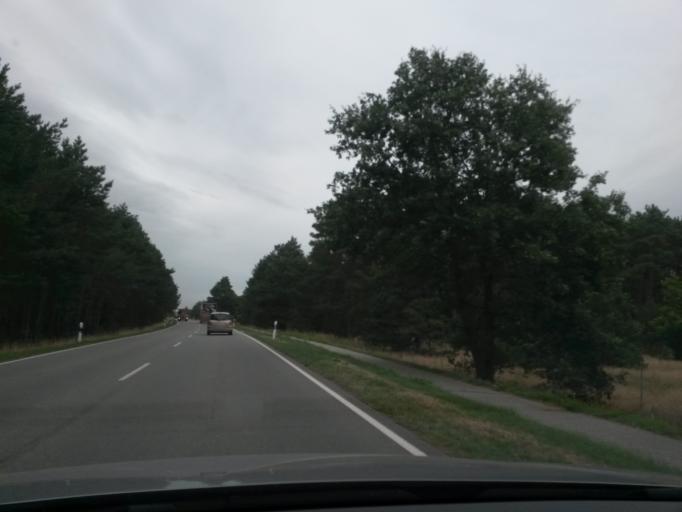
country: DE
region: Saxony-Anhalt
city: Klietz
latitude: 52.6879
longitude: 12.0672
